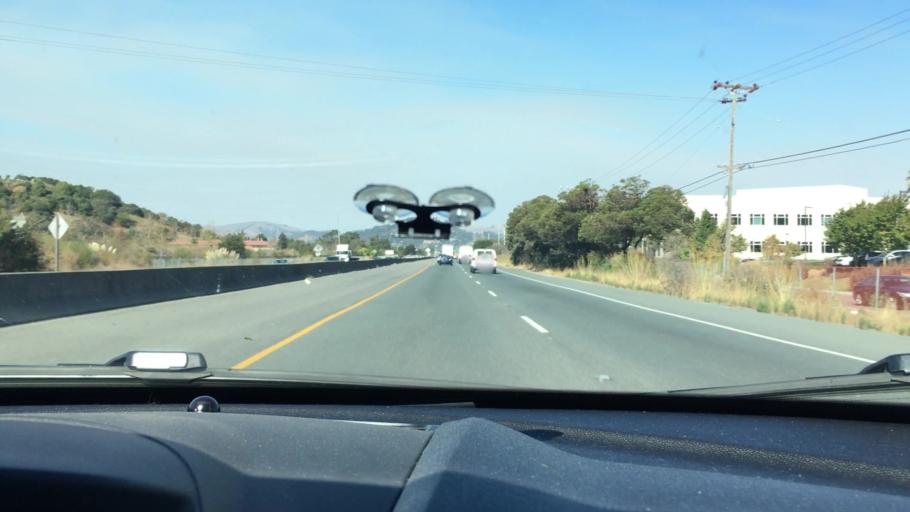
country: US
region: California
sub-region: Marin County
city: Corte Madera
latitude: 37.9473
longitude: -122.4919
